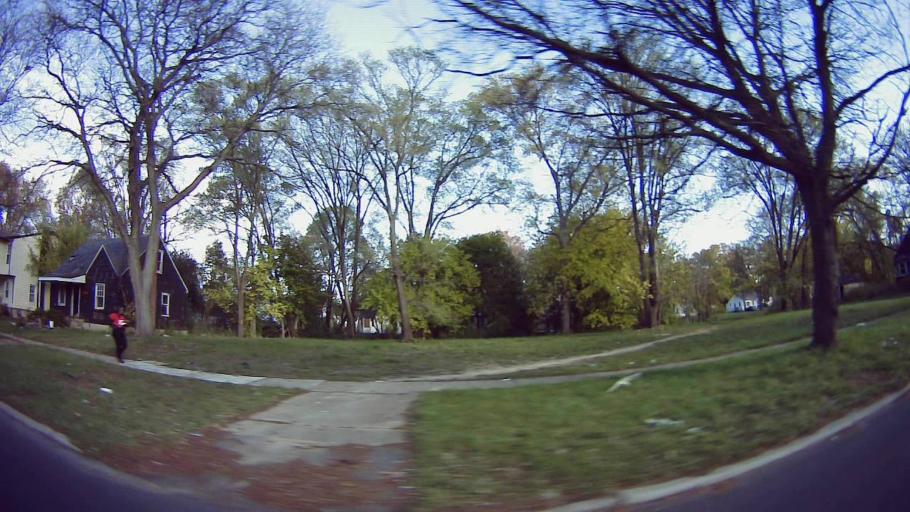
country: US
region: Michigan
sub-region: Oakland County
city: Southfield
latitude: 42.4277
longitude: -83.2387
